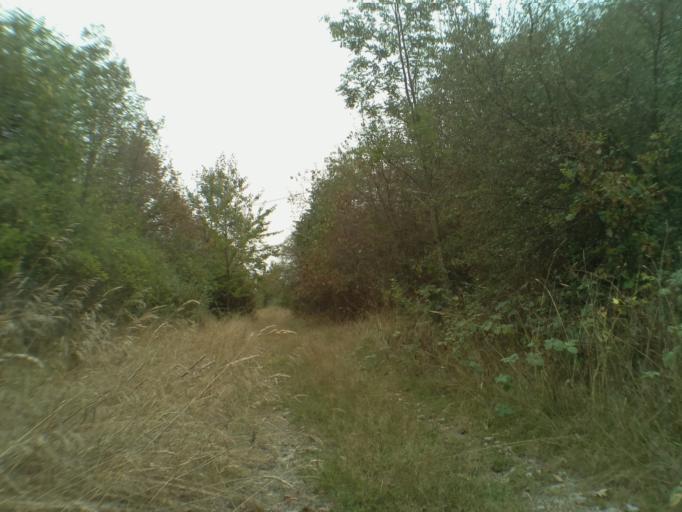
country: PL
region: Lower Silesian Voivodeship
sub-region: Powiat swidnicki
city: Strzegom
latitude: 50.9967
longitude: 16.2747
